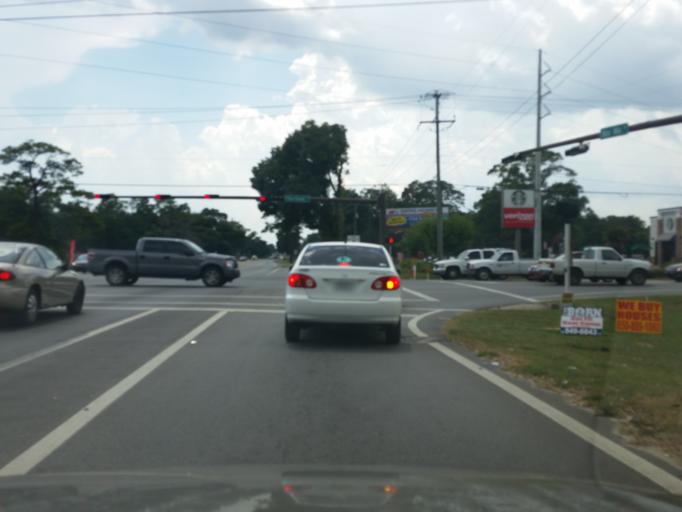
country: US
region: Florida
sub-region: Escambia County
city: Ensley
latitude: 30.5343
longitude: -87.3128
